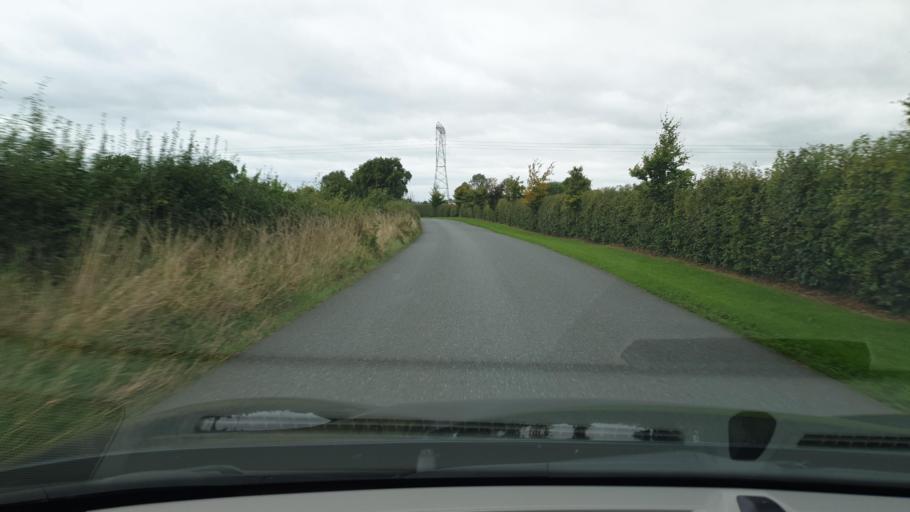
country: IE
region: Leinster
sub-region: Kildare
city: Maynooth
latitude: 53.3989
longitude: -6.6272
